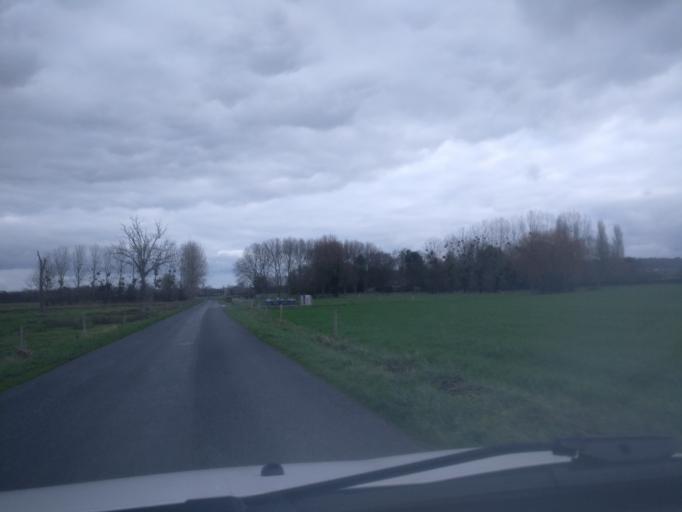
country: FR
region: Lower Normandy
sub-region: Departement de la Manche
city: Marcey-les-Greves
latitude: 48.6759
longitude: -1.4042
